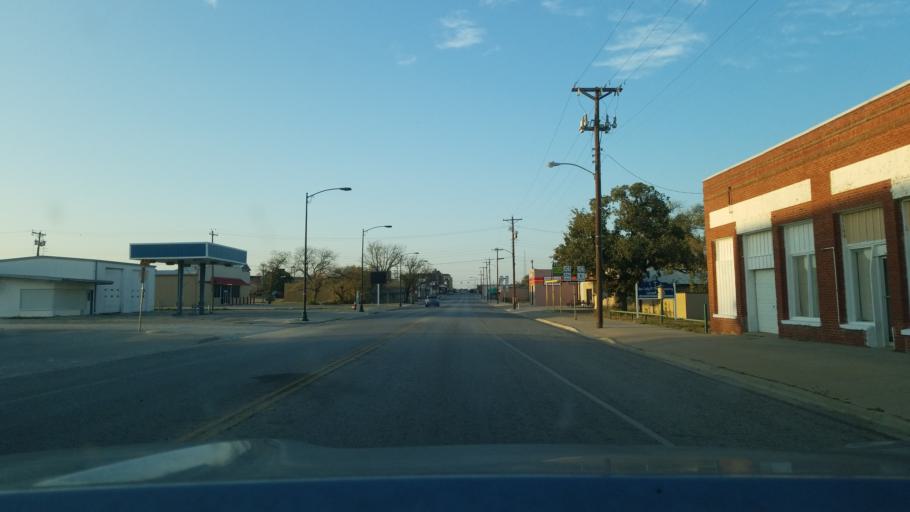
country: US
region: Texas
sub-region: Eastland County
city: Cisco
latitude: 32.3846
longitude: -98.9770
